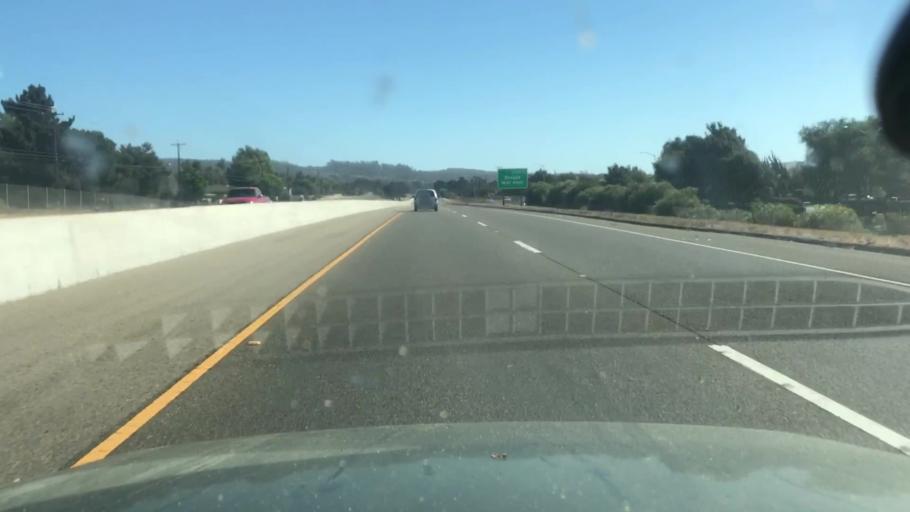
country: US
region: California
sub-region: Santa Barbara County
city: Orcutt
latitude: 34.8749
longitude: -120.4374
